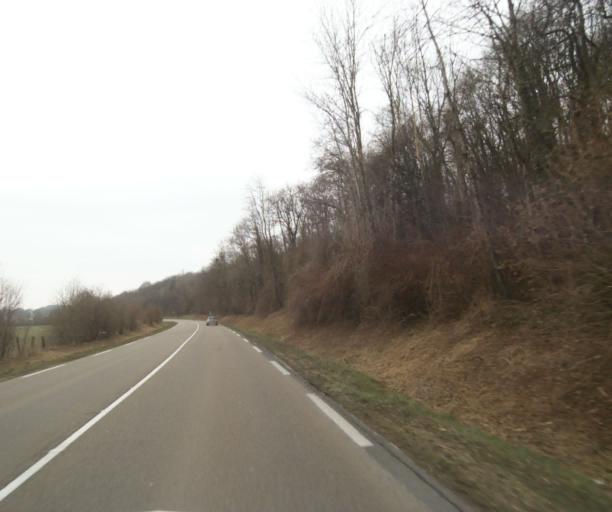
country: FR
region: Champagne-Ardenne
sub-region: Departement de la Haute-Marne
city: Bienville
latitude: 48.5971
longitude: 5.0313
